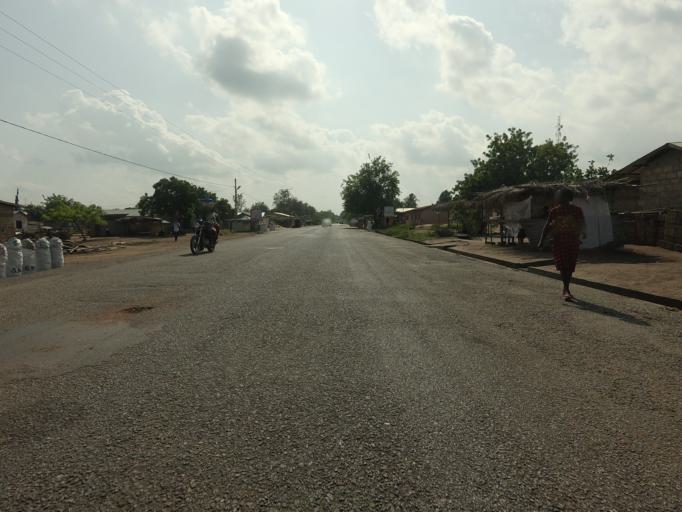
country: GH
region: Volta
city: Ho
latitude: 6.5763
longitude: 0.5874
